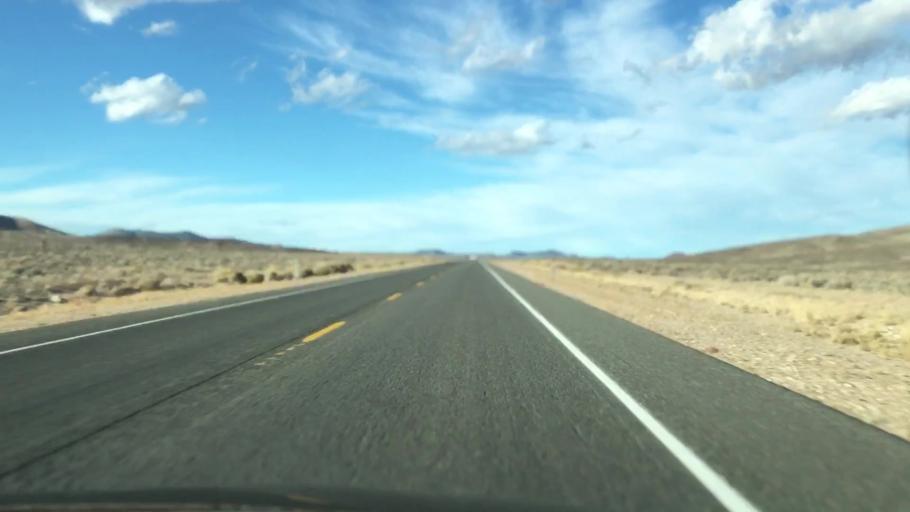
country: US
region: Nevada
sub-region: Esmeralda County
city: Goldfield
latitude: 37.5332
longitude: -117.1930
